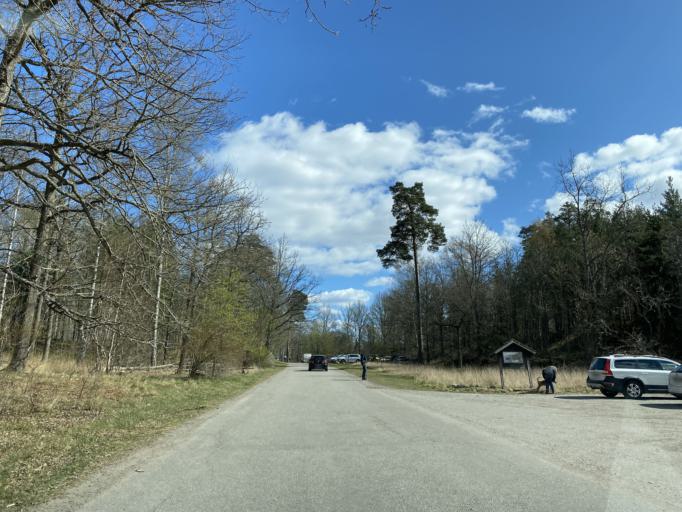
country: SE
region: Stockholm
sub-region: Nacka Kommun
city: Nacka
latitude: 59.3305
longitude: 18.1468
